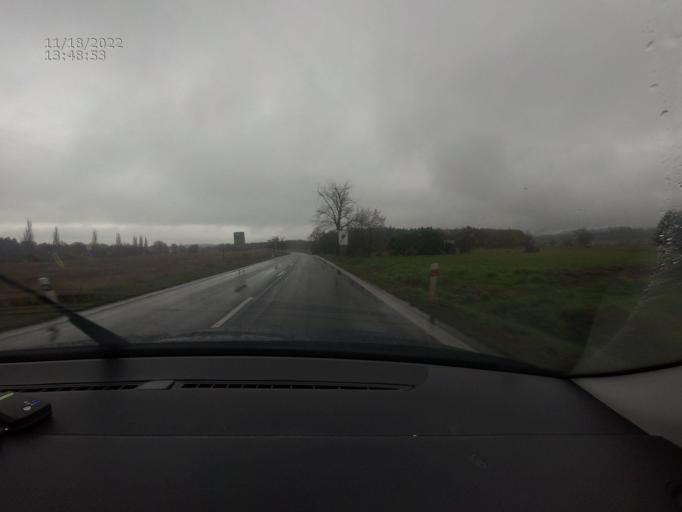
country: CZ
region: Jihocesky
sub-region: Okres Strakonice
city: Blatna
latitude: 49.4161
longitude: 13.8882
